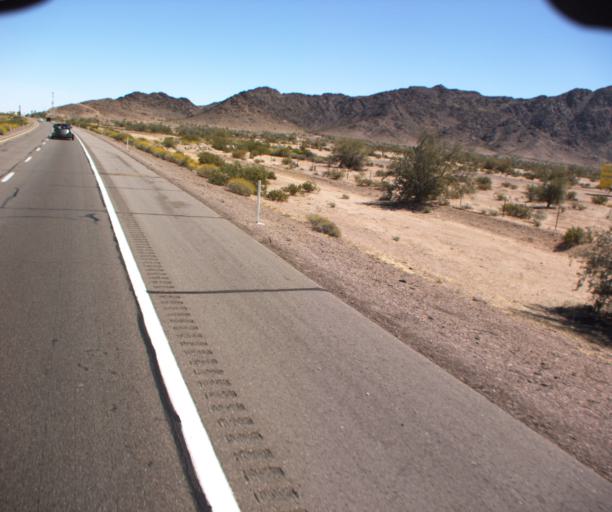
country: US
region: Arizona
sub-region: Yuma County
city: Wellton
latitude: 32.7225
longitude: -113.7618
